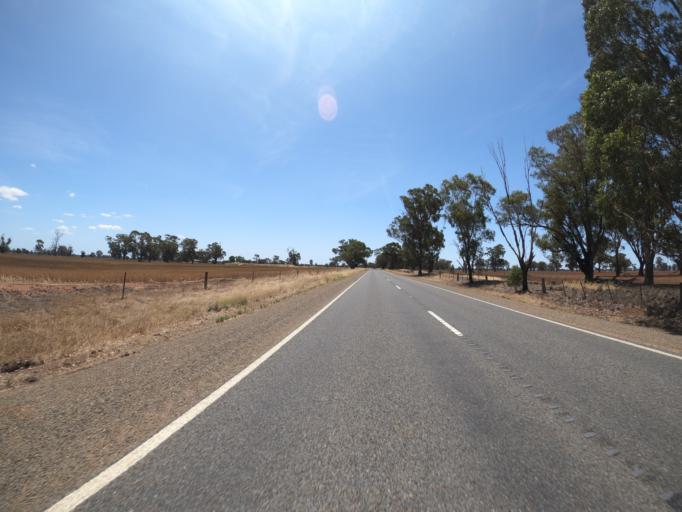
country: AU
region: Victoria
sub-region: Moira
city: Yarrawonga
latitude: -36.2045
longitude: 145.9672
